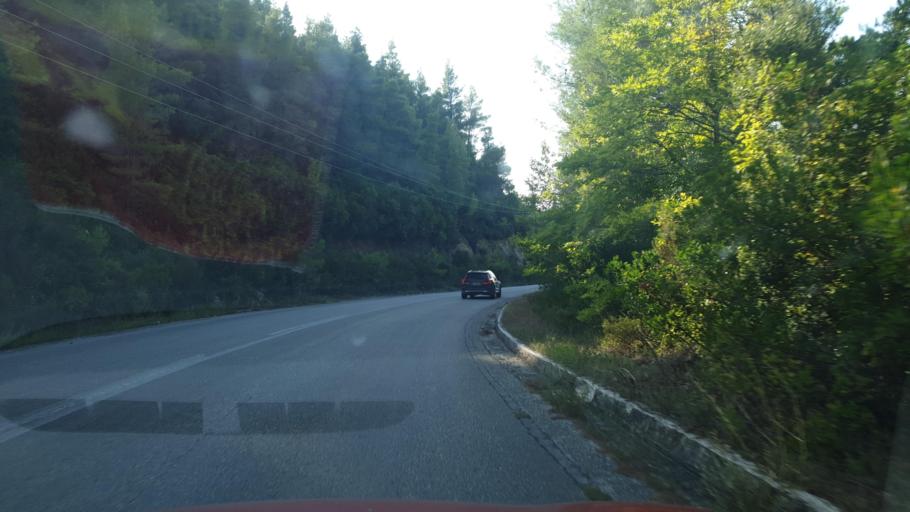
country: GR
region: Central Macedonia
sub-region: Nomos Chalkidikis
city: Neos Marmaras
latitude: 40.1607
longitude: 23.8729
